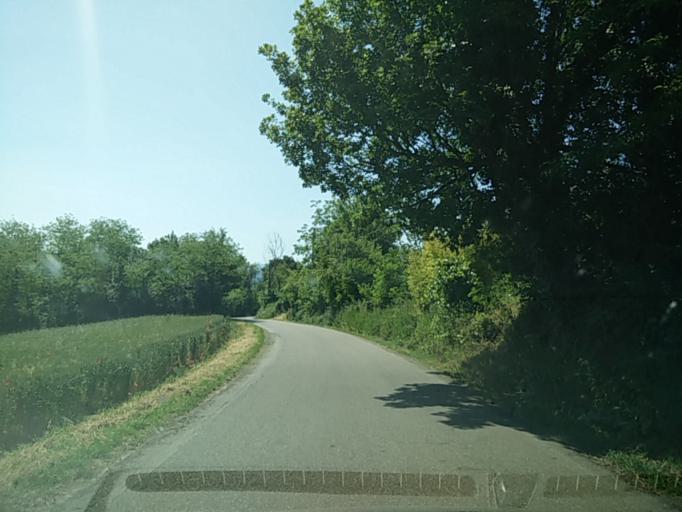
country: IT
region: Lombardy
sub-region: Provincia di Pavia
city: Godiasco
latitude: 44.8960
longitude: 9.0492
